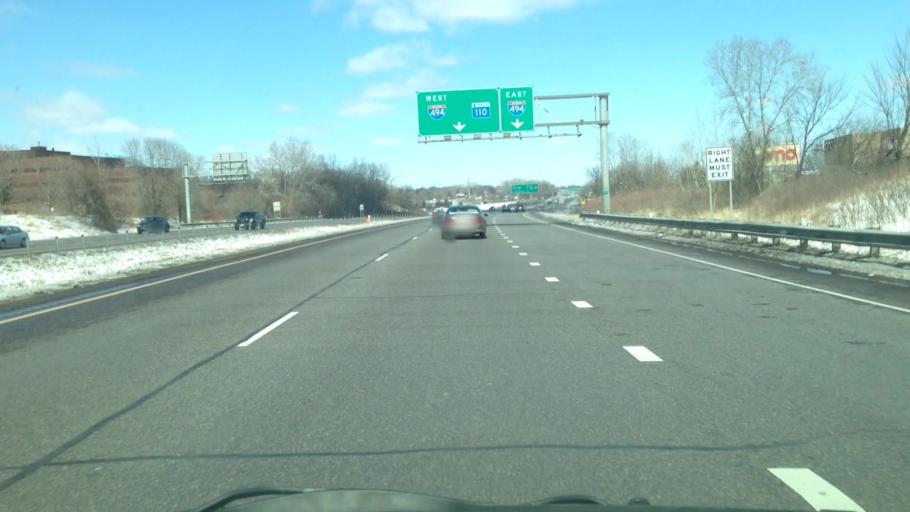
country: US
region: Minnesota
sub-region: Dakota County
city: Inver Grove Heights
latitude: 44.8669
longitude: -93.0601
